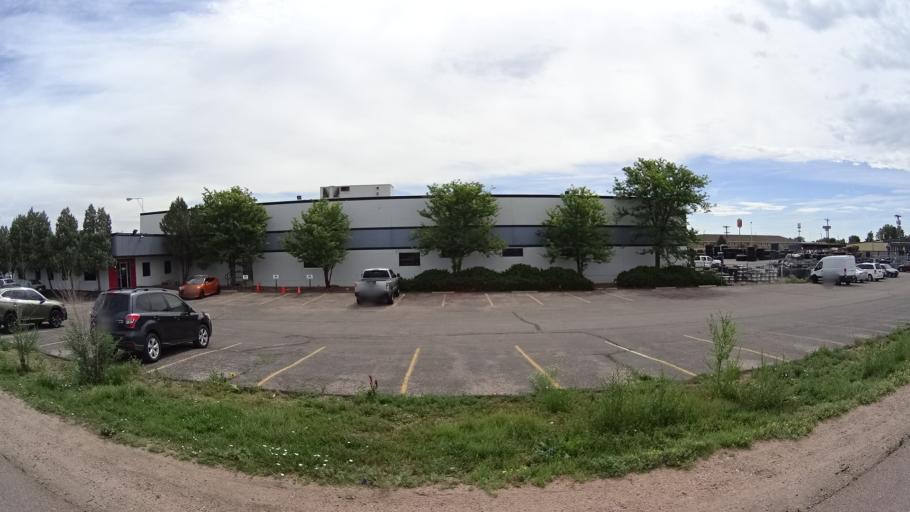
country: US
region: Colorado
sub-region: El Paso County
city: Fountain
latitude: 38.6762
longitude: -104.7150
